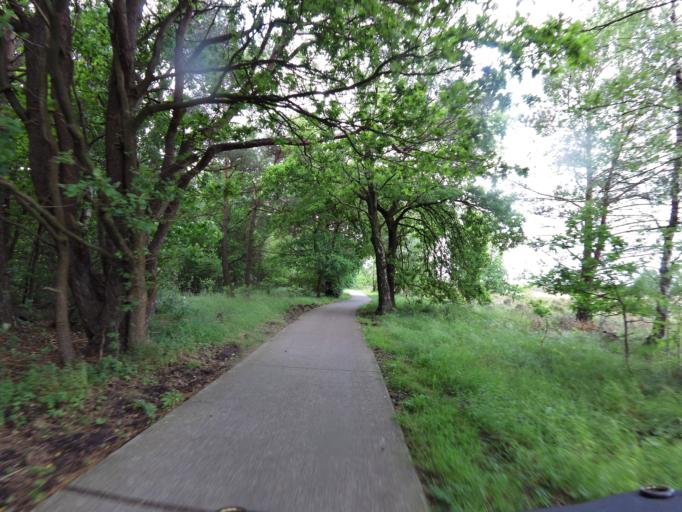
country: NL
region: Gelderland
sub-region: Gemeente Nunspeet
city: Nunspeet
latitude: 52.3208
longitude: 5.8149
